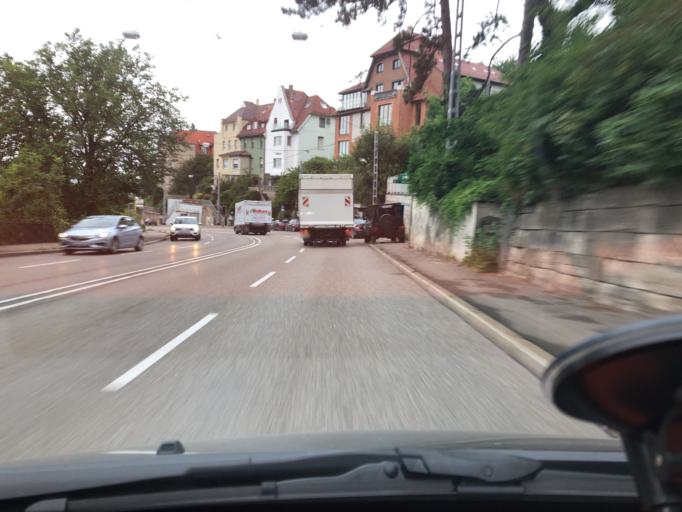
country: DE
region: Baden-Wuerttemberg
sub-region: Regierungsbezirk Stuttgart
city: Stuttgart
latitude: 48.7630
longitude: 9.1806
